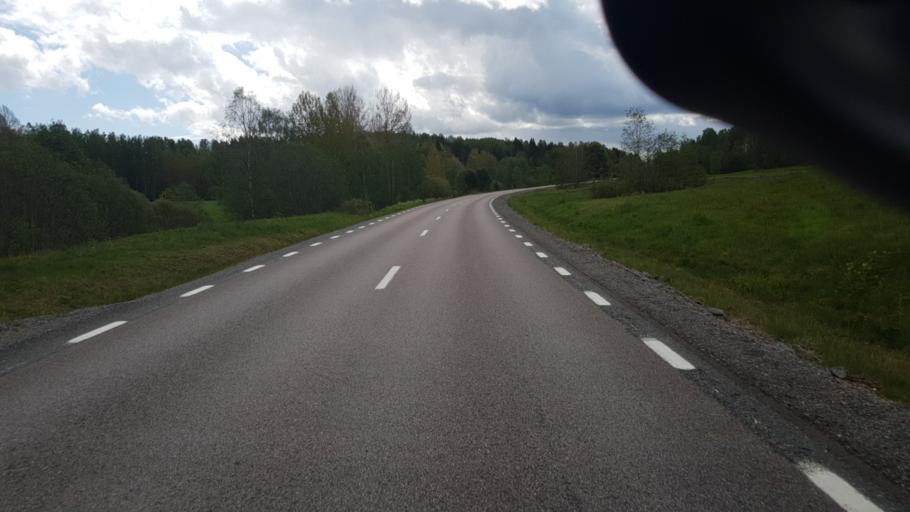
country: SE
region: Vaermland
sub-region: Arjangs Kommun
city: Arjaeng
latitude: 59.6327
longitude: 12.1376
